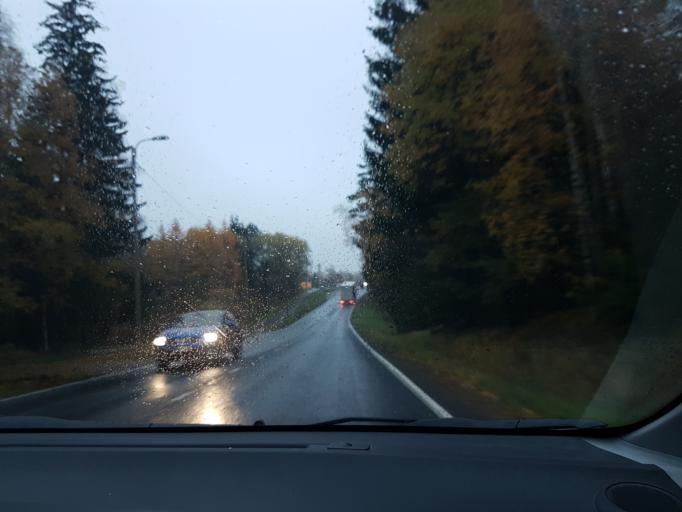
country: FI
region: Uusimaa
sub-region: Helsinki
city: Jaervenpaeae
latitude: 60.5259
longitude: 25.1015
